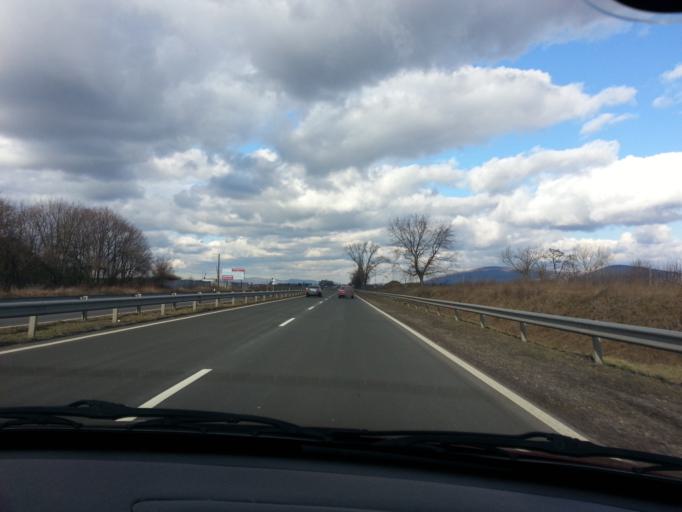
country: HU
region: Heves
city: Lorinci
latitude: 47.7467
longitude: 19.6637
